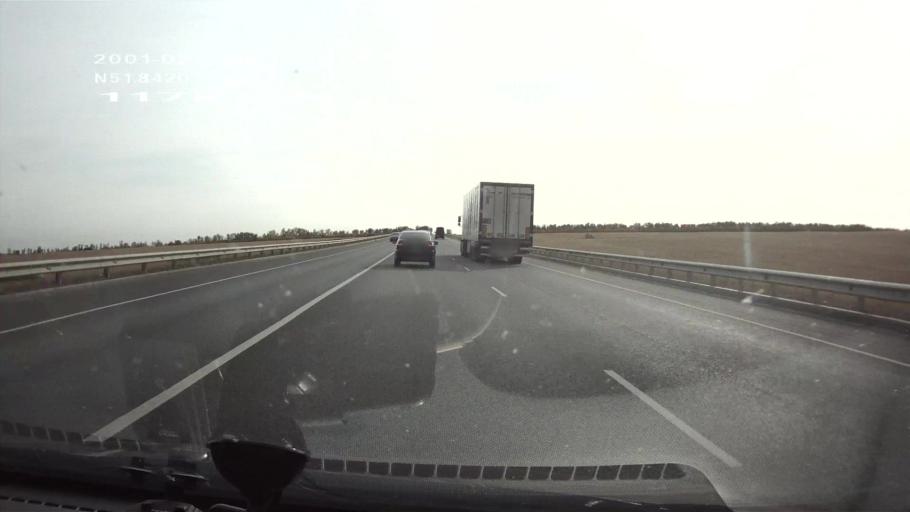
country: RU
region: Saratov
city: Yelshanka
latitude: 51.8410
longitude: 46.4787
